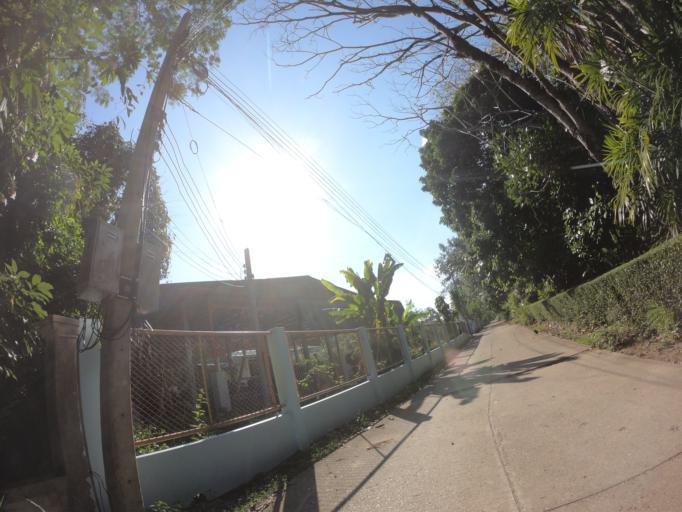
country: TH
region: Chiang Mai
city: Chiang Mai
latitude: 18.7577
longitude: 98.9828
